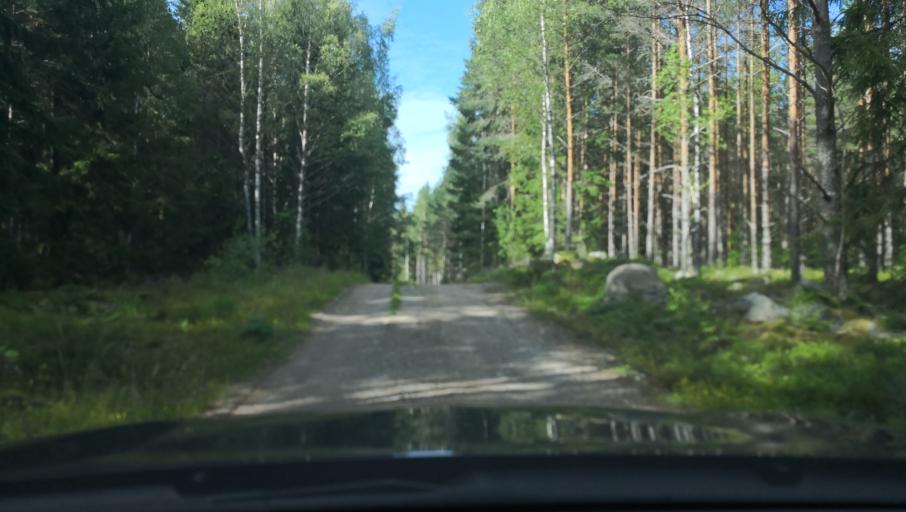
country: SE
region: Vaestmanland
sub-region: Surahammars Kommun
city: Surahammar
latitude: 59.6706
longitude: 16.1084
